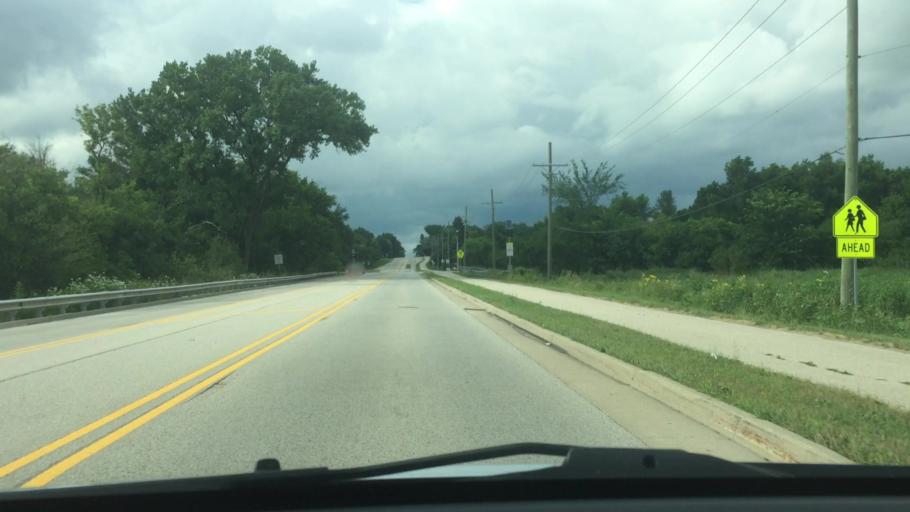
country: US
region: Illinois
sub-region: McHenry County
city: Crystal Lake
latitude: 42.2684
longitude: -88.3208
